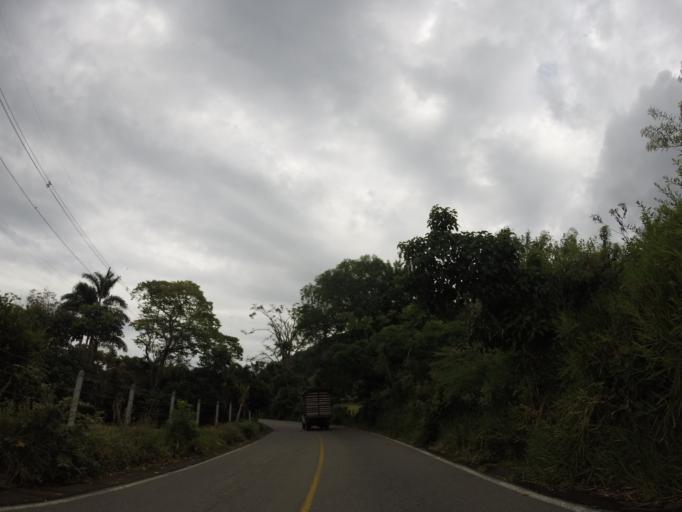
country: CO
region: Caldas
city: Victoria
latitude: 5.3200
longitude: -74.9251
